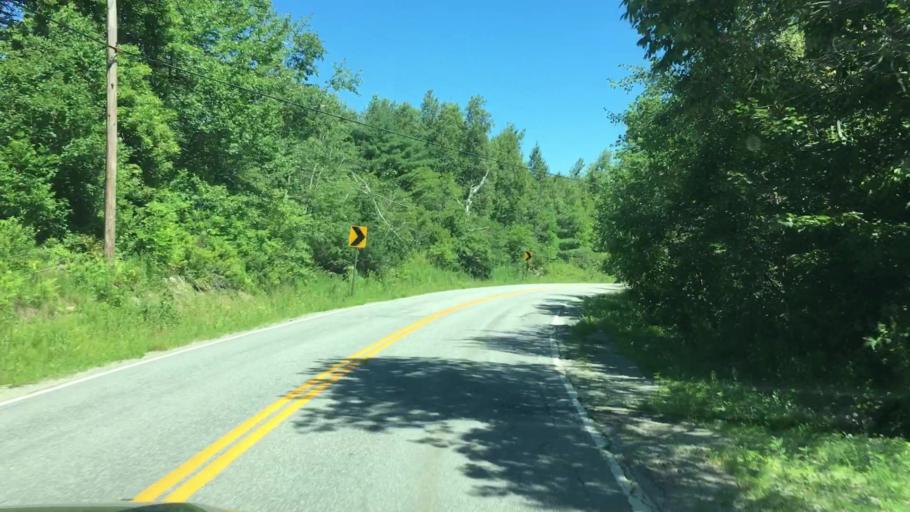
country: US
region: Maine
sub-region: Hancock County
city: Penobscot
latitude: 44.4989
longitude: -68.6816
